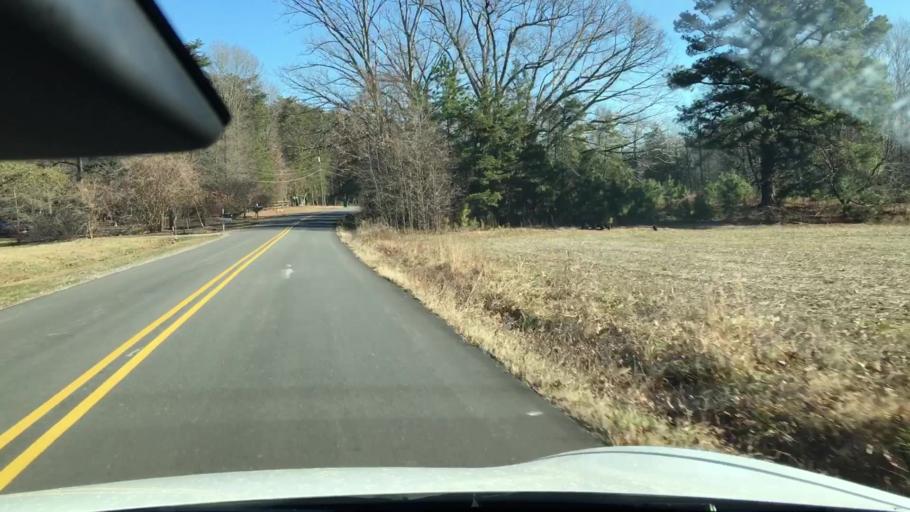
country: US
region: Virginia
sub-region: Powhatan County
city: Powhatan
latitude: 37.5706
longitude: -77.7807
